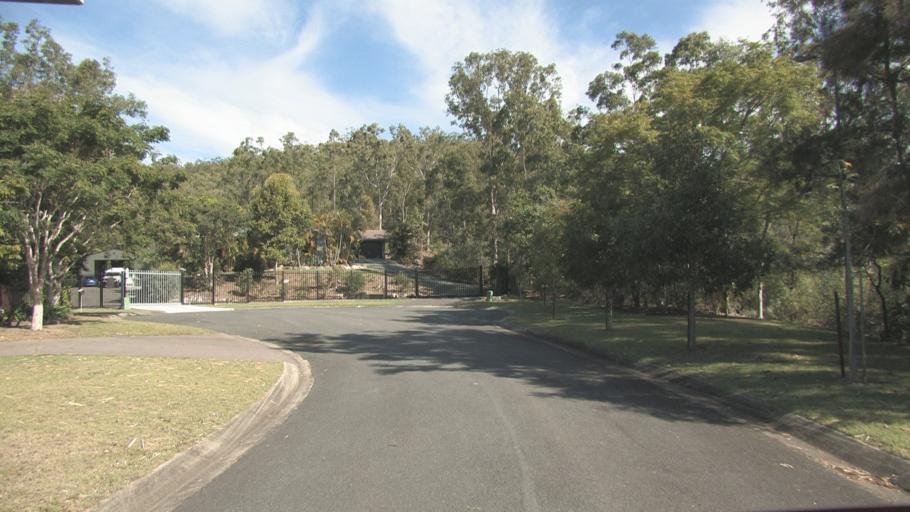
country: AU
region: Queensland
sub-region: Logan
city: Windaroo
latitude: -27.7620
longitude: 153.1789
